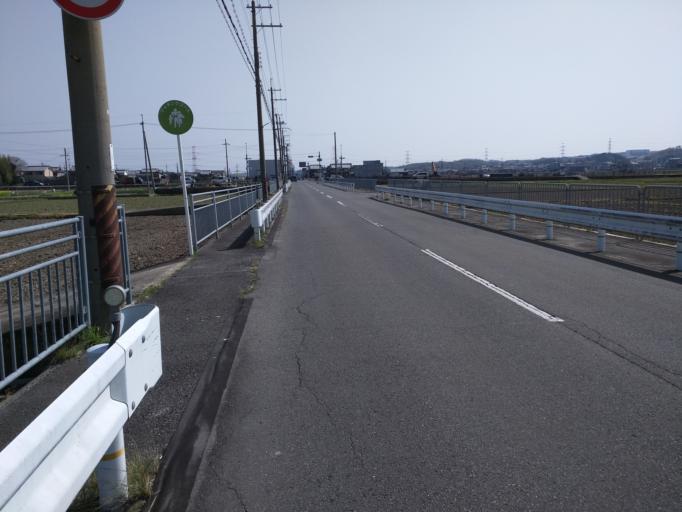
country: JP
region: Kyoto
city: Tanabe
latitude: 34.7700
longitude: 135.7975
